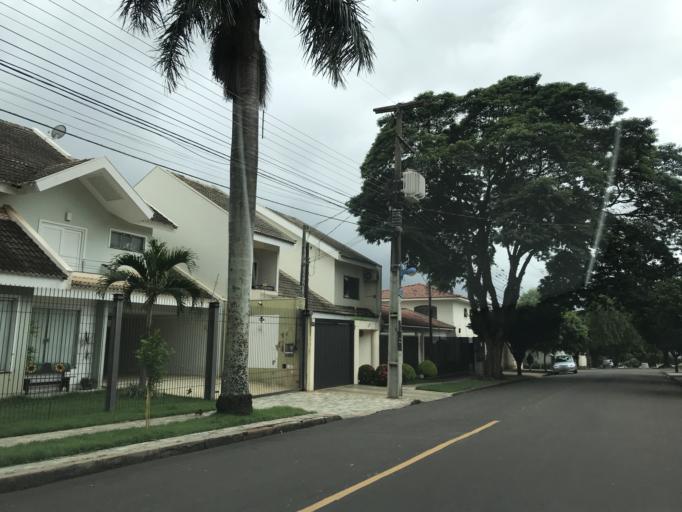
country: BR
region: Parana
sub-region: Maringa
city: Maringa
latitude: -23.4426
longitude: -51.9578
